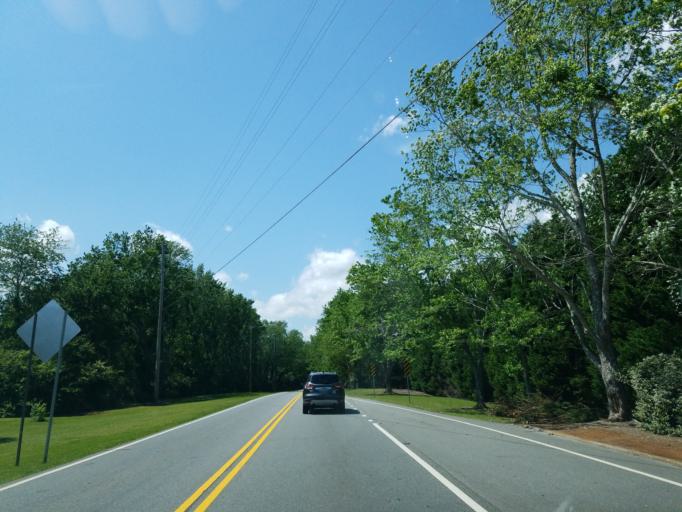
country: US
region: Georgia
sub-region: Fulton County
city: Roswell
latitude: 34.0659
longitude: -84.3490
